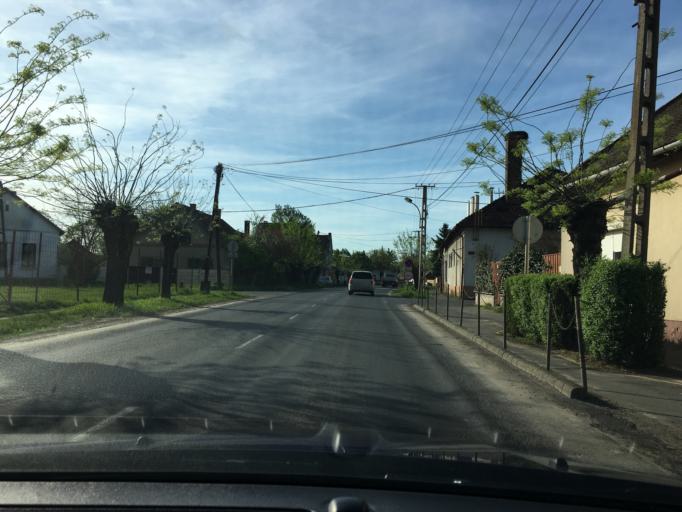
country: HU
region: Bekes
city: Mezobereny
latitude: 46.8291
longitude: 21.0283
